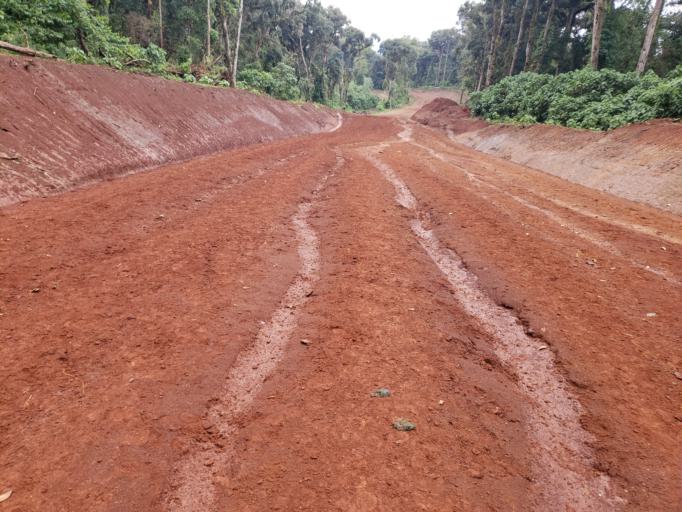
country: ET
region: Oromiya
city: Dodola
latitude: 6.5914
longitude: 39.4120
